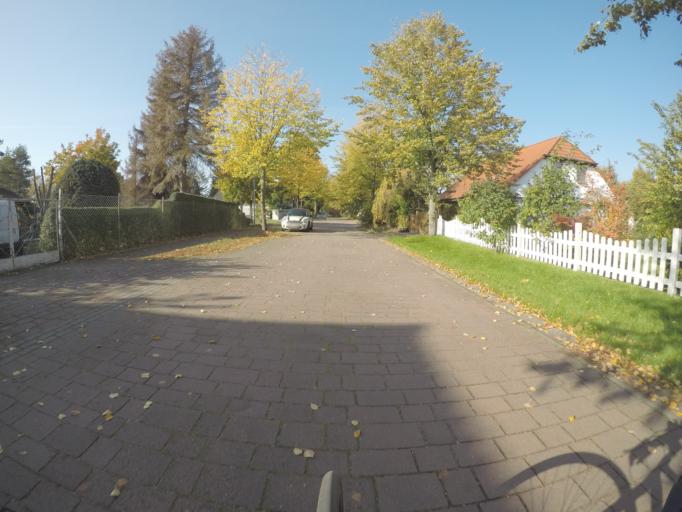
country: DE
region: Brandenburg
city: Oranienburg
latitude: 52.7315
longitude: 13.2512
